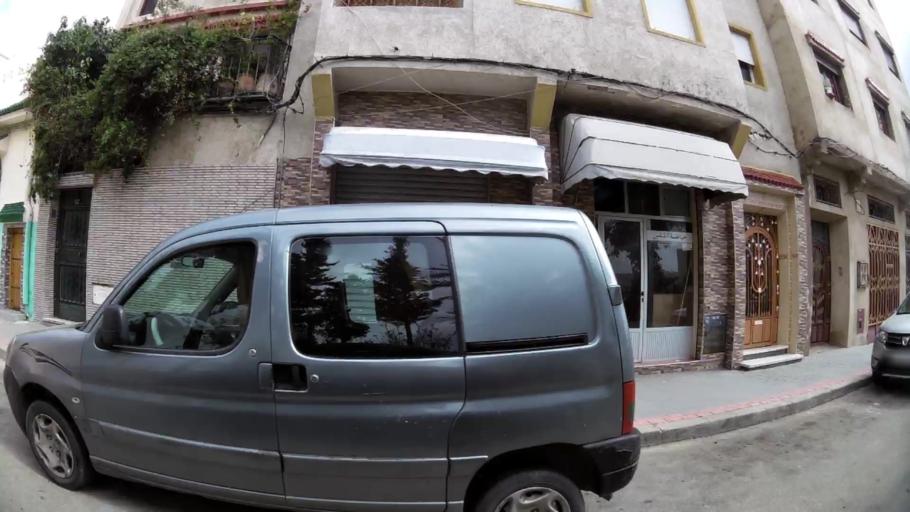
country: MA
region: Tanger-Tetouan
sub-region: Tanger-Assilah
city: Tangier
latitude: 35.7680
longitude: -5.8234
